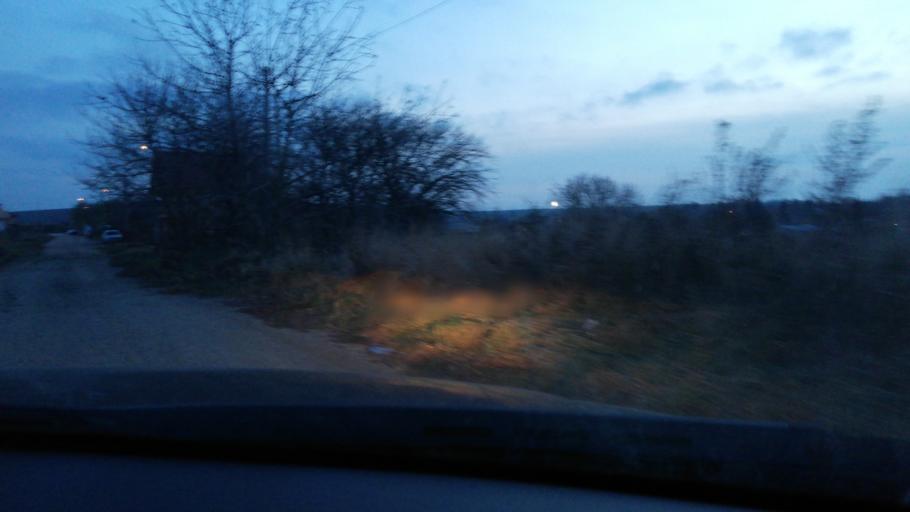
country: SK
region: Nitriansky
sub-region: Okres Nitra
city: Nitra
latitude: 48.3179
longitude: 17.9943
